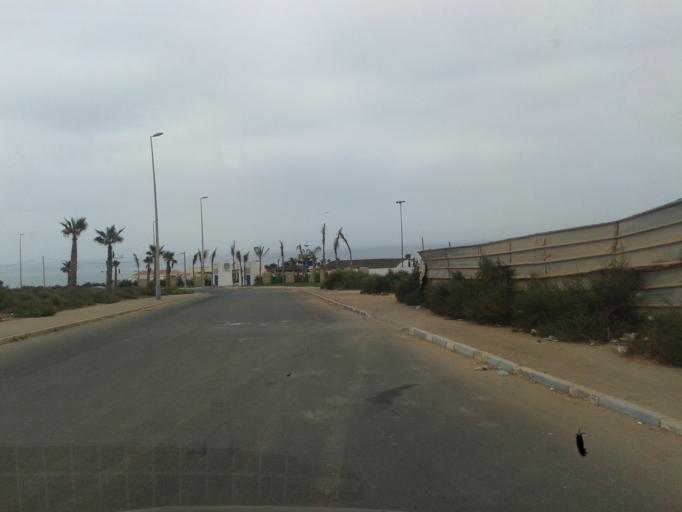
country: MA
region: Souss-Massa-Draa
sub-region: Agadir-Ida-ou-Tnan
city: Aourir
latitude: 30.4595
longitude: -9.6647
